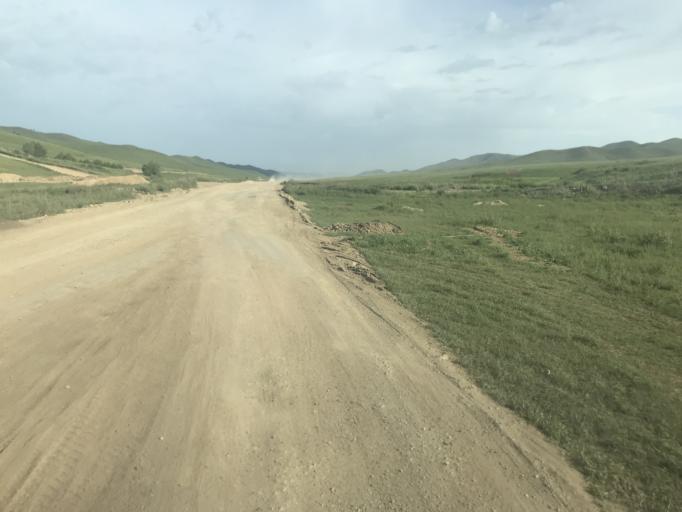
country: MN
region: Central Aimak
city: Javhlant
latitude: 48.7361
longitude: 106.1318
